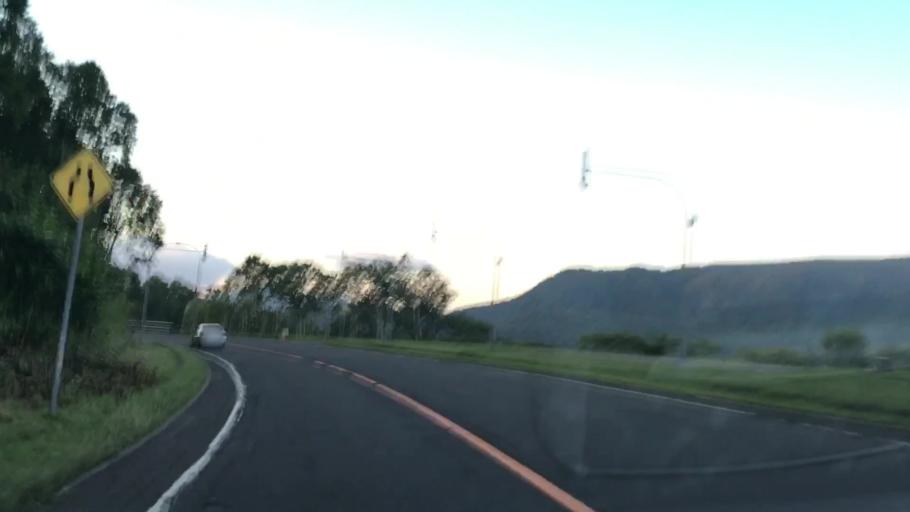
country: JP
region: Hokkaido
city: Sapporo
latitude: 42.8761
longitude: 141.1468
